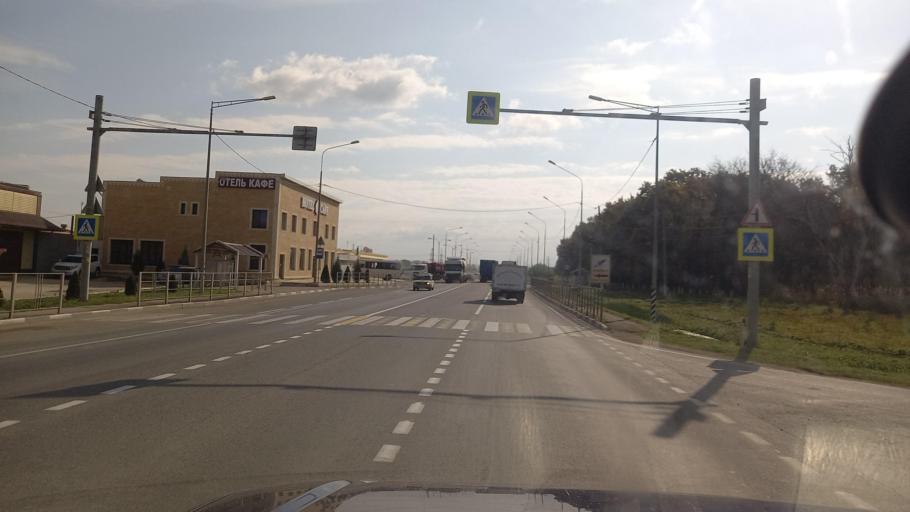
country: RU
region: Krasnodarskiy
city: Novoukrainskiy
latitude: 44.9091
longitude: 38.0218
